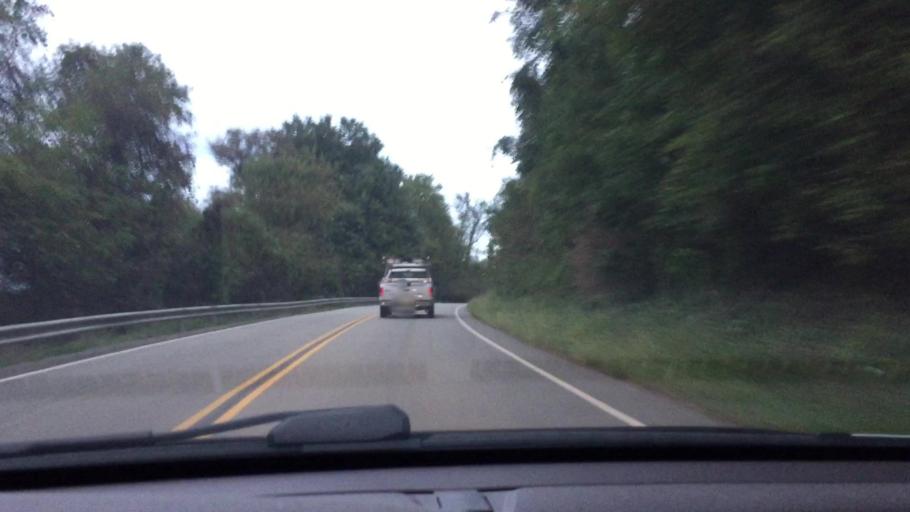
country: US
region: Pennsylvania
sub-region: Westmoreland County
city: Fellsburg
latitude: 40.1840
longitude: -79.8030
